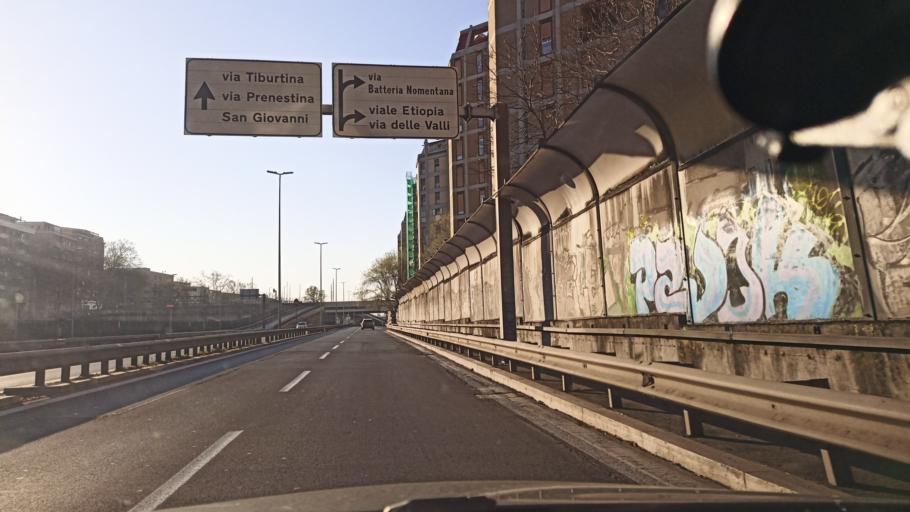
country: IT
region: Latium
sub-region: Citta metropolitana di Roma Capitale
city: Rome
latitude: 41.9319
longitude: 12.5239
